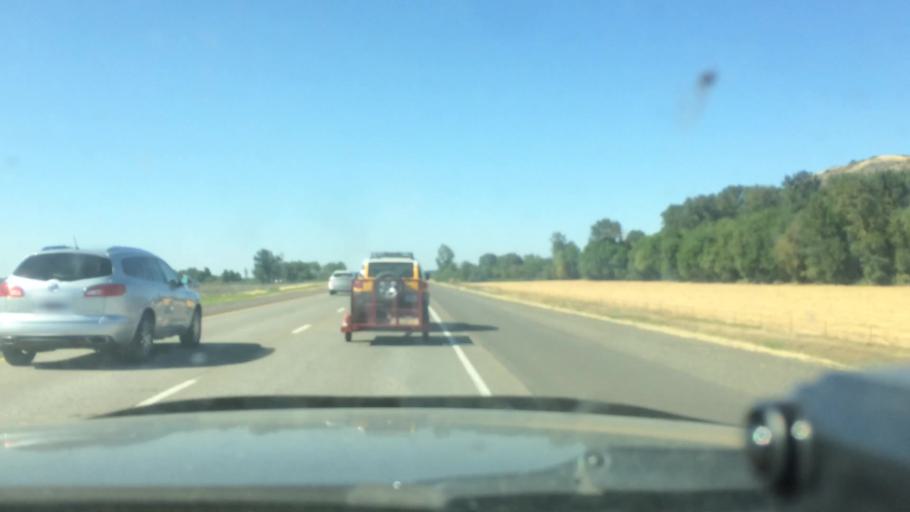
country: US
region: Oregon
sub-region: Linn County
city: Brownsville
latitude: 44.4485
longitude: -123.0600
